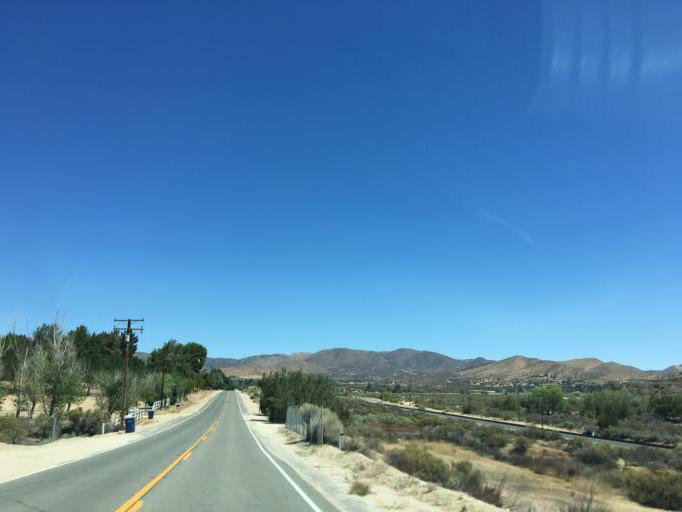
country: US
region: California
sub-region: Los Angeles County
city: Acton
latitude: 34.4603
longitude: -118.1980
